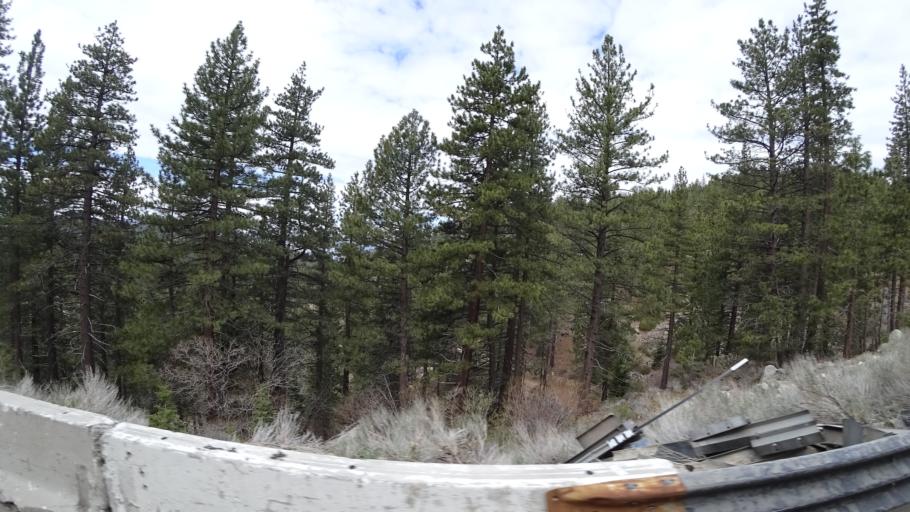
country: US
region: Nevada
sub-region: Washoe County
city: Incline Village
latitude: 39.1307
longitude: -119.9318
